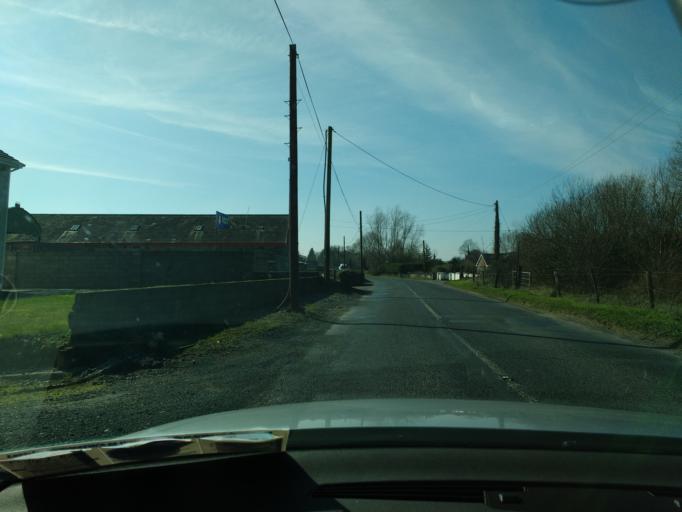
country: IE
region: Munster
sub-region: County Limerick
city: Castleconnell
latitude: 52.6968
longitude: -8.4631
